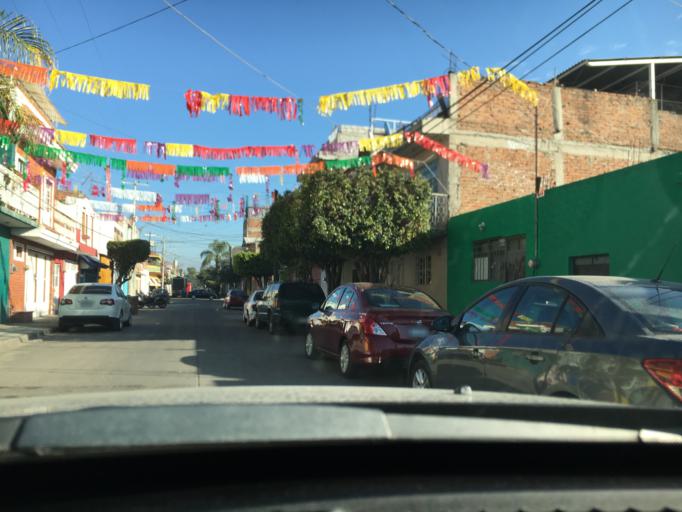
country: MX
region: Guanajuato
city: Leon
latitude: 21.1271
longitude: -101.6521
